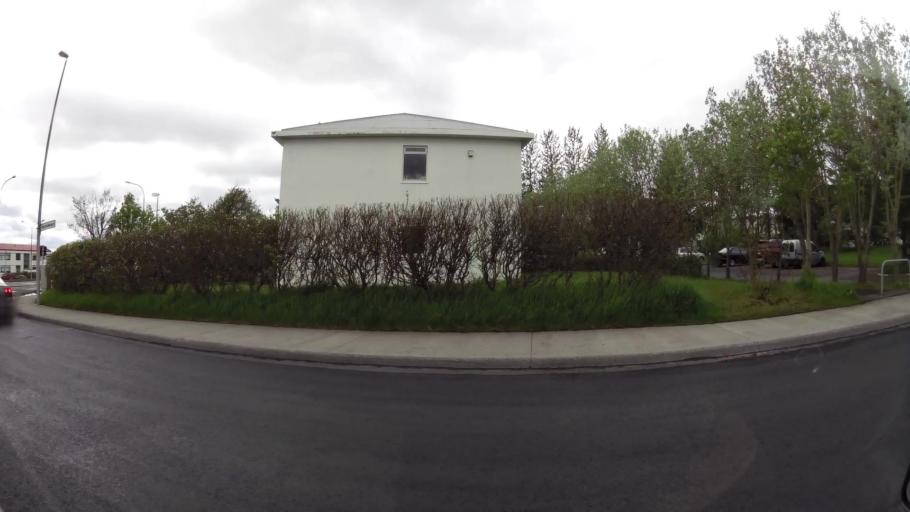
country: IS
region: Capital Region
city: Reykjavik
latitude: 64.1221
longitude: -21.8694
